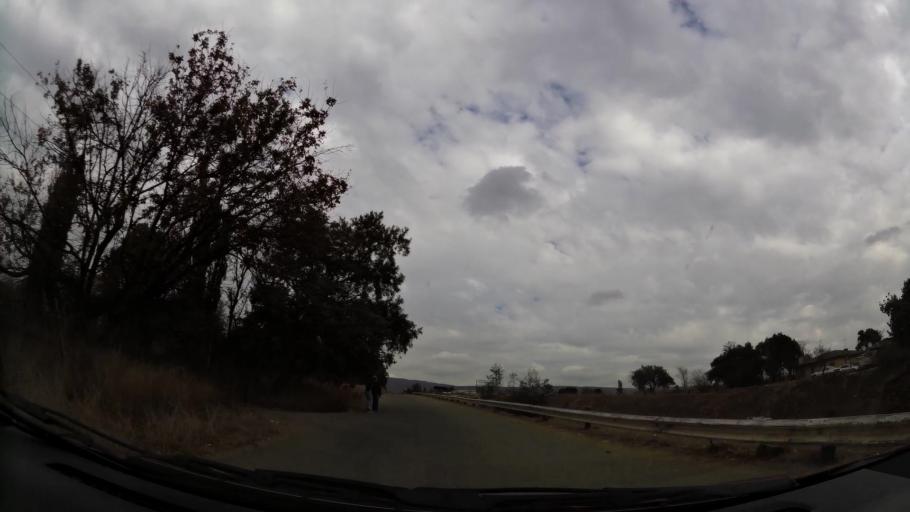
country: ZA
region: Gauteng
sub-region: West Rand District Municipality
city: Muldersdriseloop
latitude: -26.0402
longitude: 27.8443
